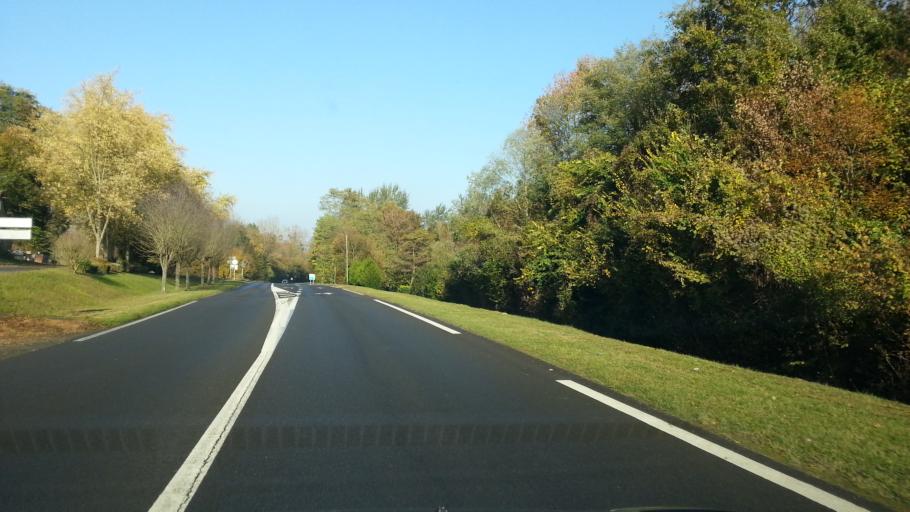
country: FR
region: Picardie
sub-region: Departement de l'Oise
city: Balagny-sur-Therain
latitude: 49.3034
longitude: 2.3310
